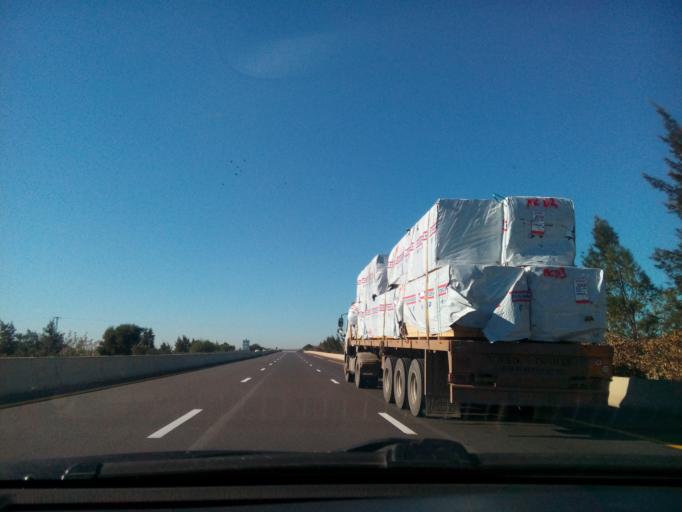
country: DZ
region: Relizane
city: Djidiouia
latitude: 35.9166
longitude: 0.7568
